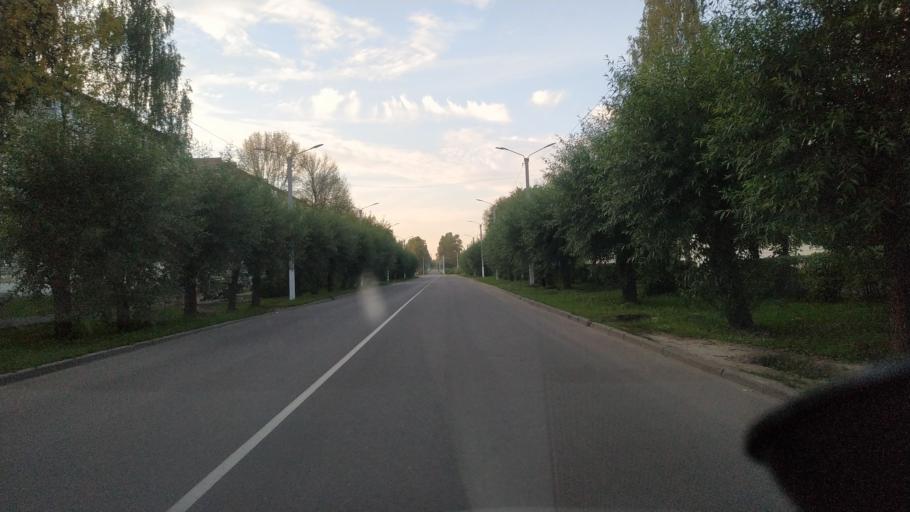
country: RU
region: Moskovskaya
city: Roshal'
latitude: 55.6644
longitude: 39.8526
